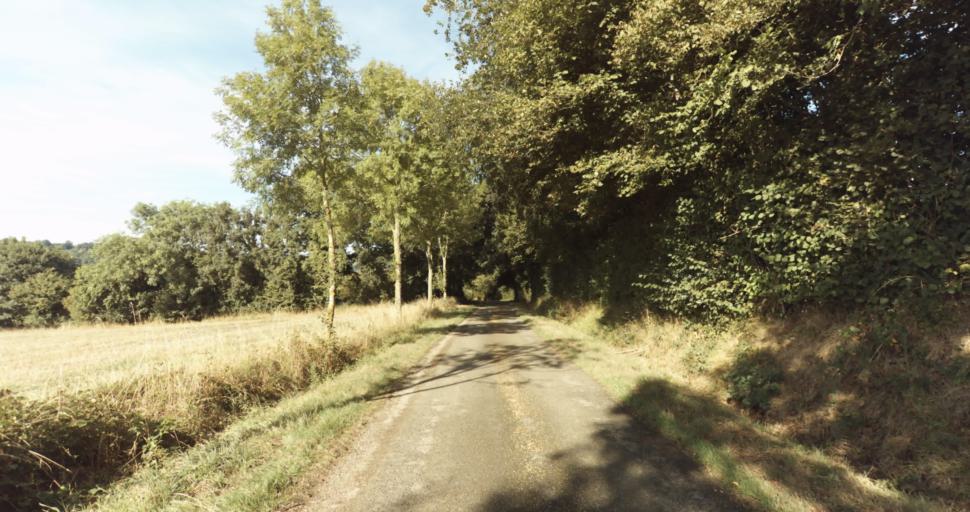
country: FR
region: Lower Normandy
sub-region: Departement du Calvados
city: Livarot
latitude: 48.9364
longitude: 0.1218
